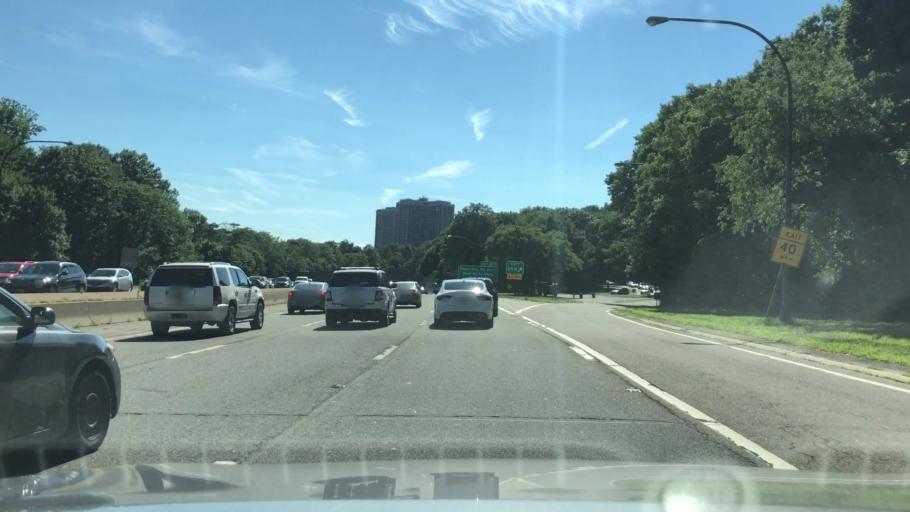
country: US
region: New York
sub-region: Nassau County
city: North New Hyde Park
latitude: 40.7610
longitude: -73.7003
